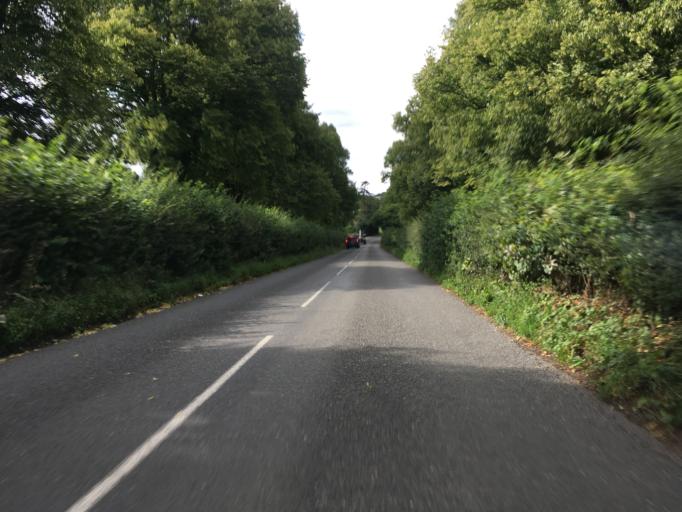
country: GB
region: England
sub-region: Hampshire
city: Overton
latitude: 51.1685
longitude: -1.2318
